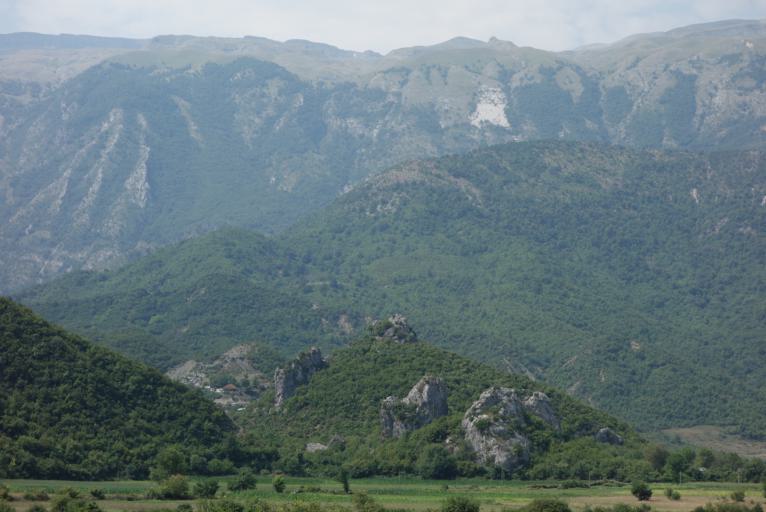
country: AL
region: Gjirokaster
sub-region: Rrethi i Permetit
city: Petran
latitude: 40.2081
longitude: 20.4122
